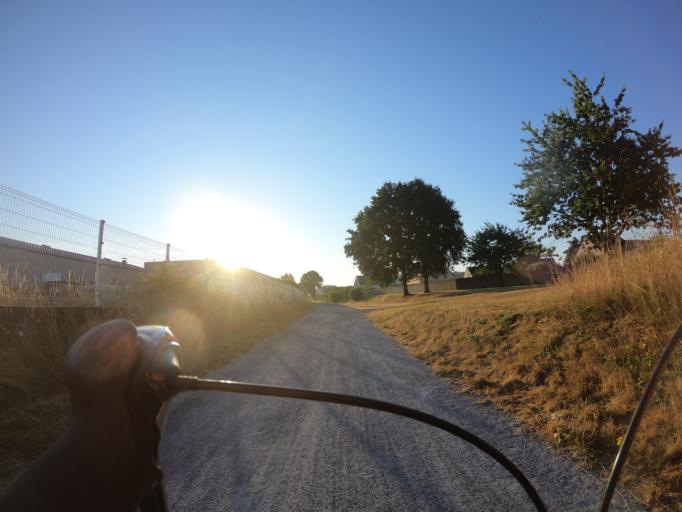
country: FR
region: Lower Normandy
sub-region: Departement de la Manche
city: Ducey
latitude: 48.6234
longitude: -1.2919
